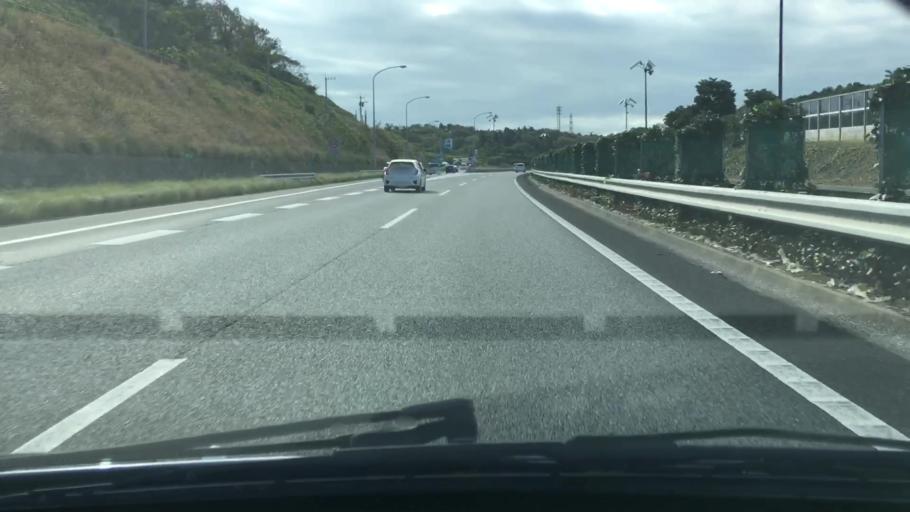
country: JP
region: Chiba
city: Ichihara
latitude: 35.4617
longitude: 140.0859
